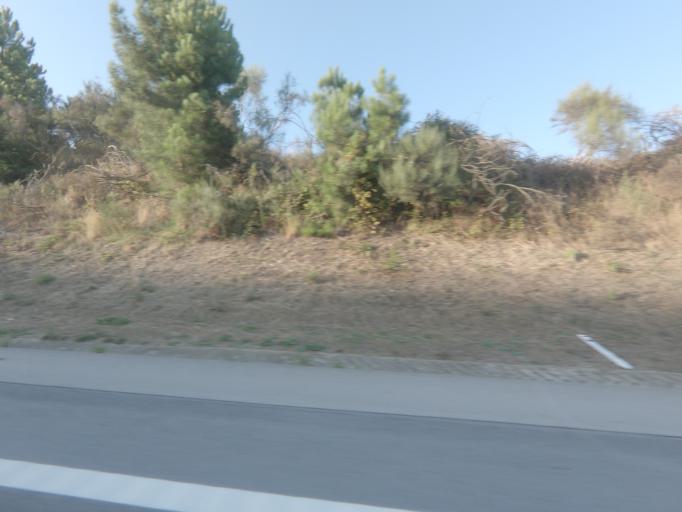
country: PT
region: Vila Real
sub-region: Vila Real
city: Vila Real
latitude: 41.3128
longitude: -7.6890
